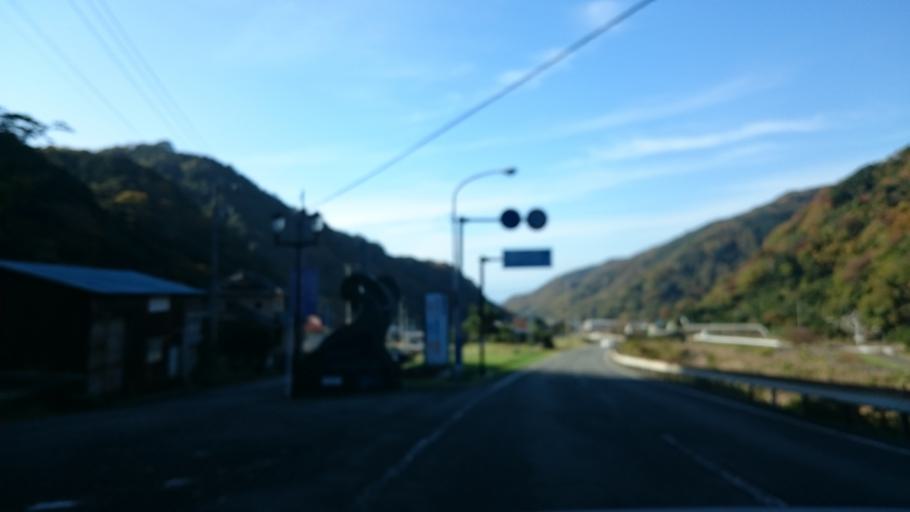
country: JP
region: Shizuoka
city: Heda
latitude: 34.9649
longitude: 138.8066
